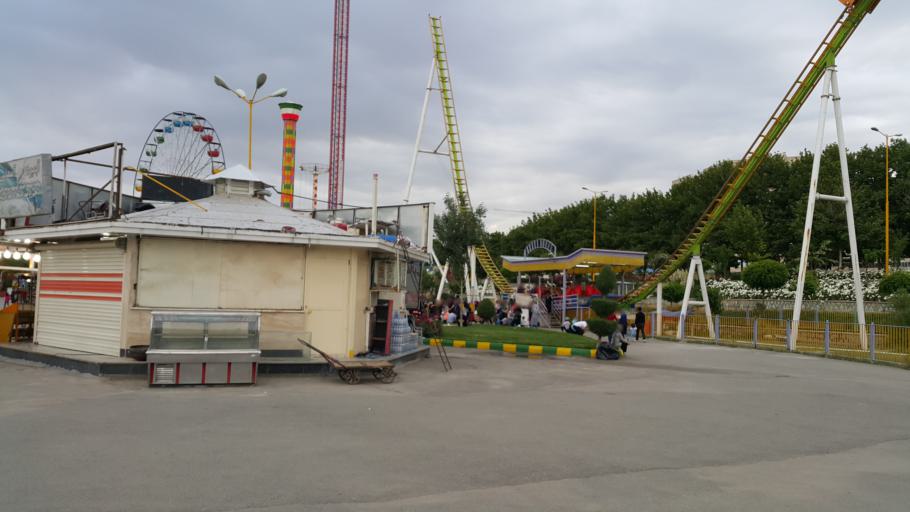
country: IR
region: Tehran
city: Tehran
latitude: 35.7216
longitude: 51.2956
